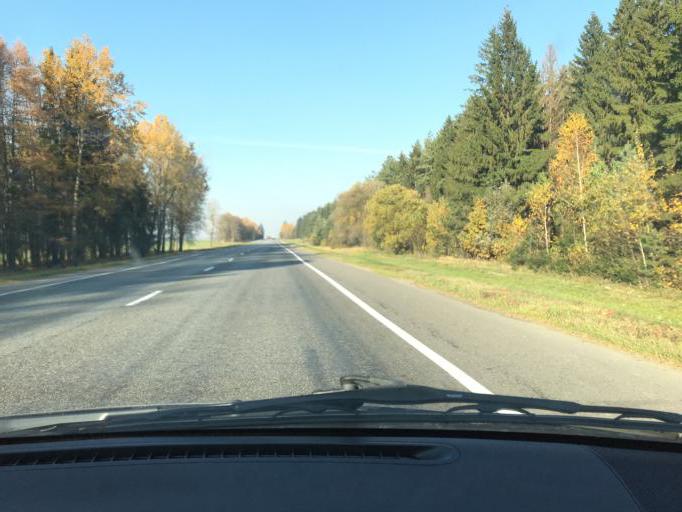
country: BY
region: Mogilev
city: Shklow
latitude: 54.2870
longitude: 30.4489
